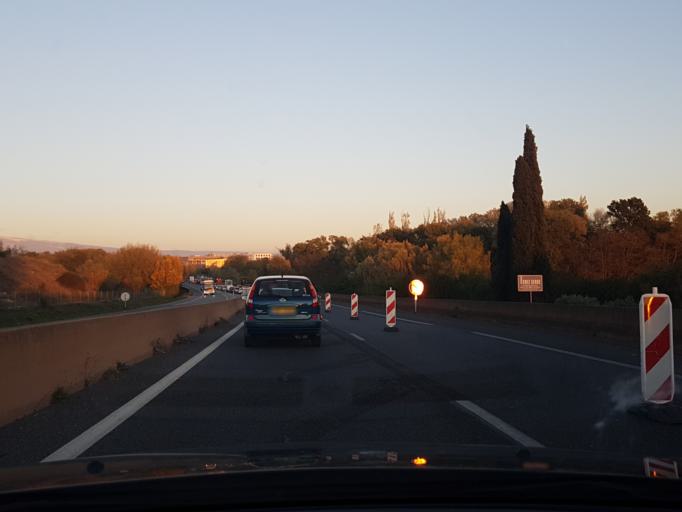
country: FR
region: Provence-Alpes-Cote d'Azur
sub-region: Departement du Vaucluse
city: Monteux
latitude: 44.0449
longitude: 5.0160
